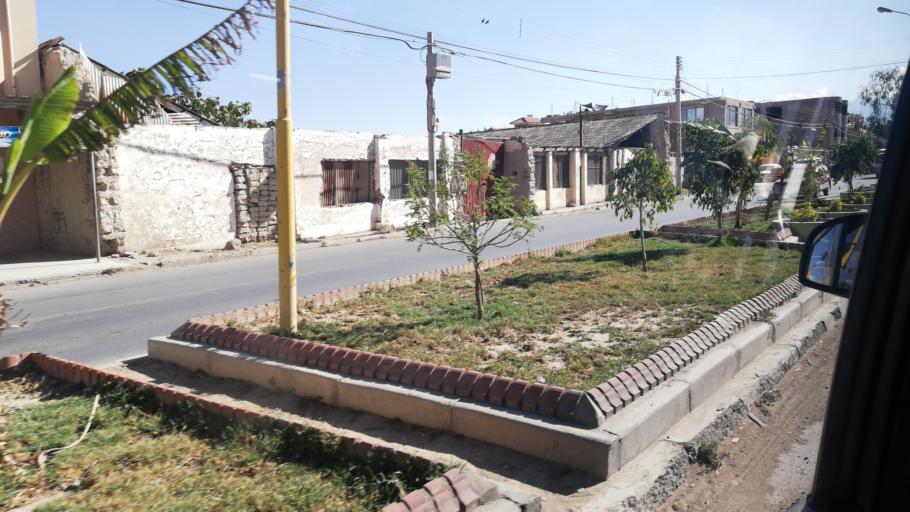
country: BO
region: Cochabamba
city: Cochabamba
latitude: -17.3936
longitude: -66.2490
